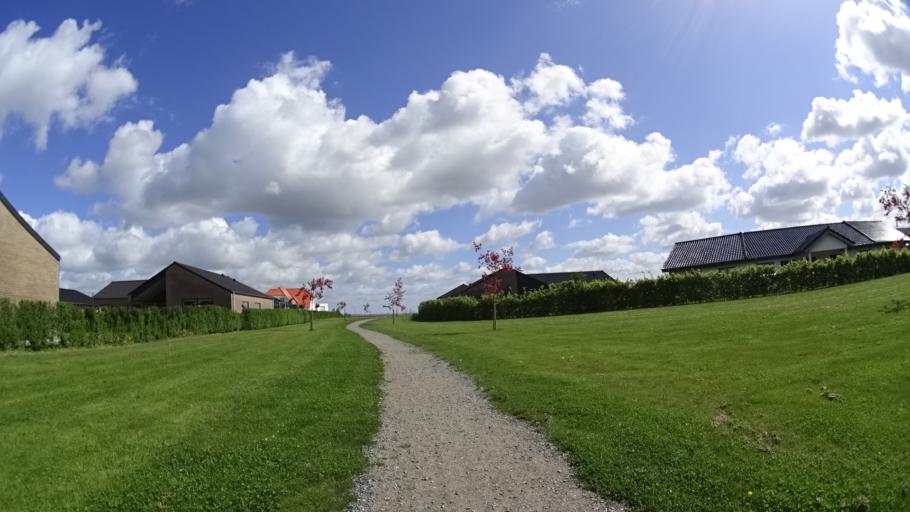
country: DK
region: Central Jutland
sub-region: Arhus Kommune
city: Stavtrup
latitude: 56.1266
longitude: 10.1069
